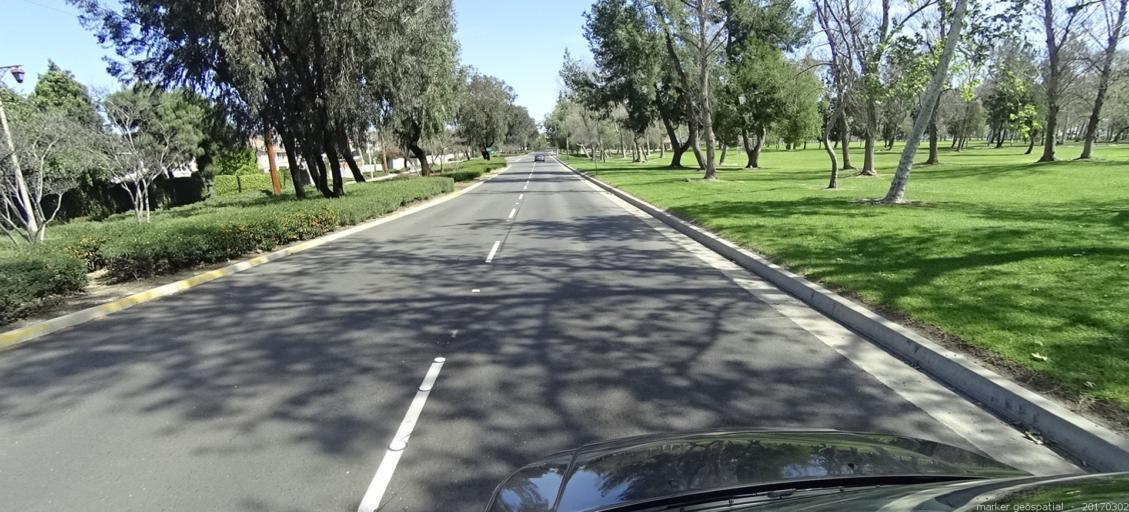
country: US
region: California
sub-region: Orange County
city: Yorba Linda
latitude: 33.8726
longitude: -117.7600
